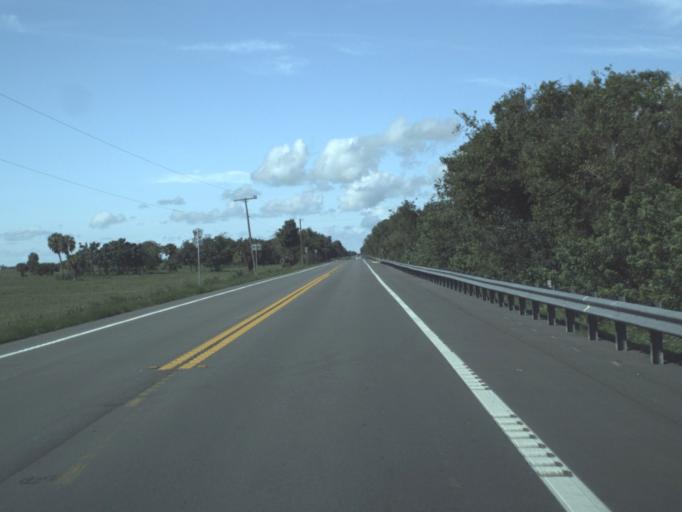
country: US
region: Florida
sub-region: Glades County
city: Buckhead Ridge
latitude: 27.1297
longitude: -80.9044
